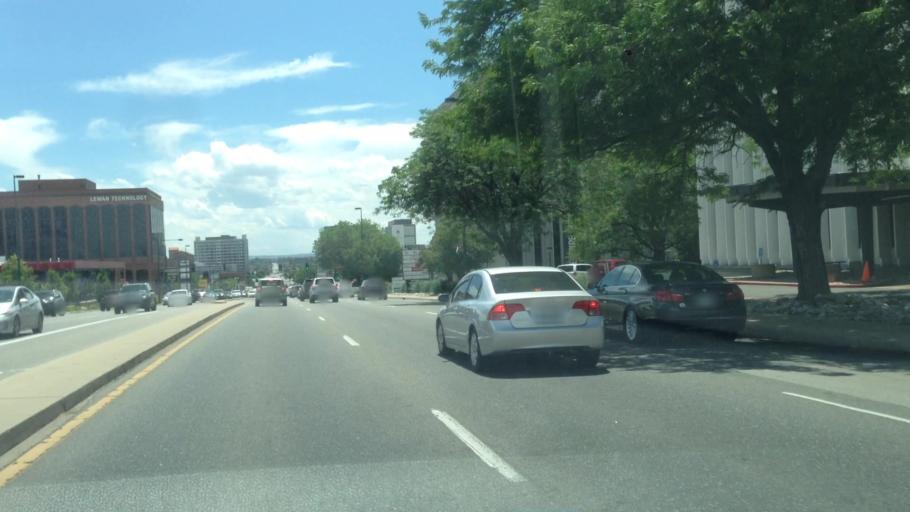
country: US
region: Colorado
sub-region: Arapahoe County
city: Glendale
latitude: 39.6928
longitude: -104.9407
